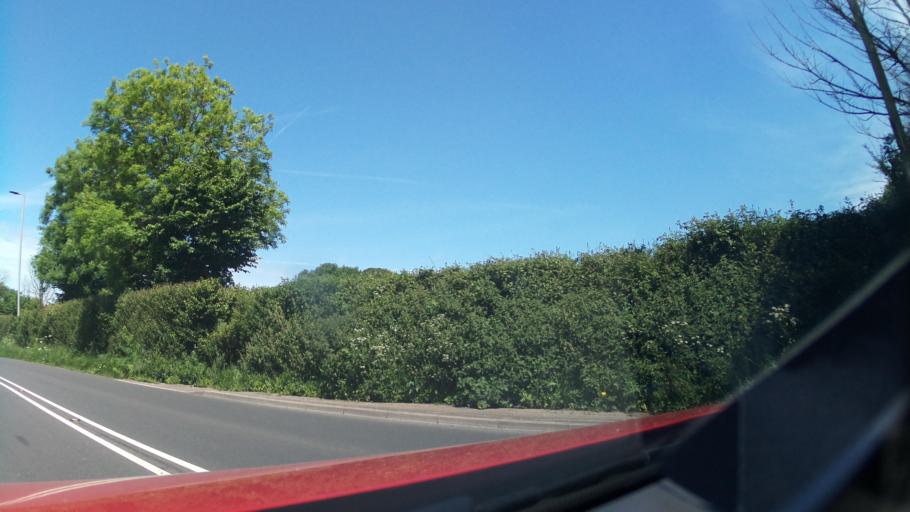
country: GB
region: England
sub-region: Devon
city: Starcross
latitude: 50.6562
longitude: -3.4207
